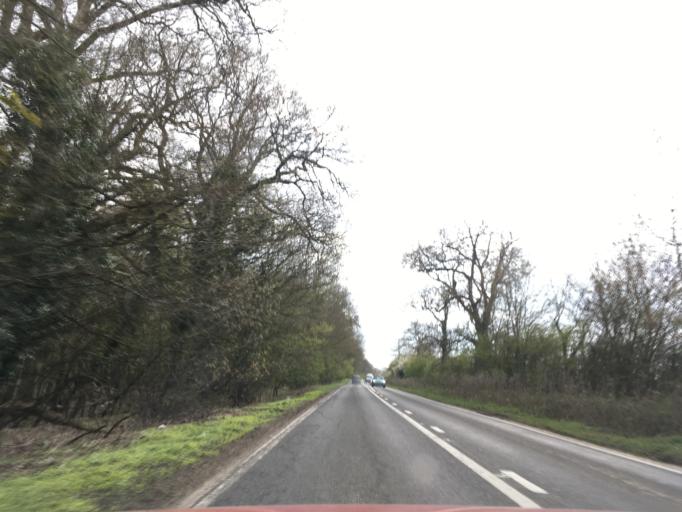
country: GB
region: England
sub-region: Oxfordshire
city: North Leigh
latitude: 51.8108
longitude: -1.4355
